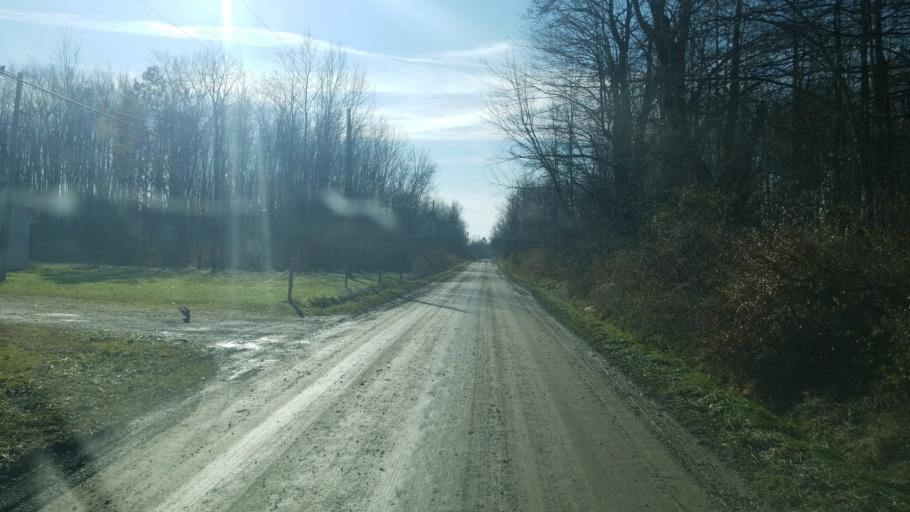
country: US
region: Ohio
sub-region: Ashtabula County
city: Jefferson
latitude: 41.7271
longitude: -80.6845
